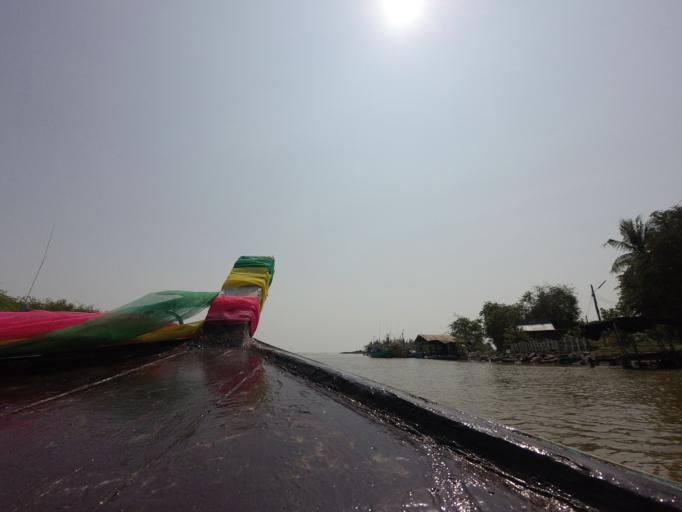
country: TH
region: Prachuap Khiri Khan
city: Kui Buri
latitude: 12.1340
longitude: 99.9679
